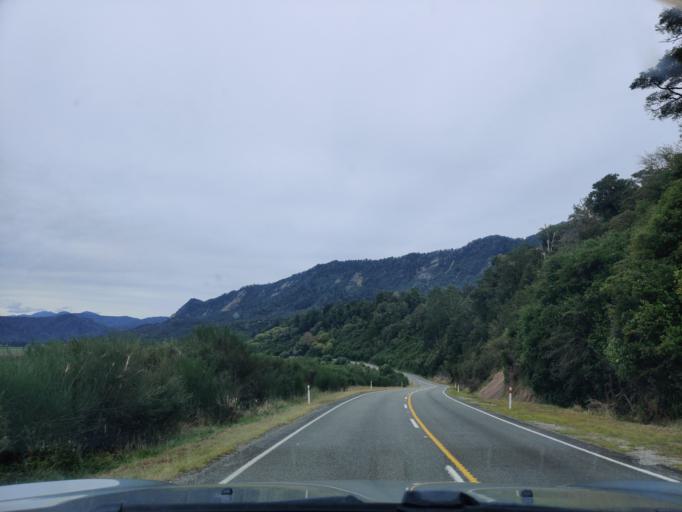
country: NZ
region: West Coast
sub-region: Buller District
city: Westport
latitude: -41.8594
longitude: 171.8626
